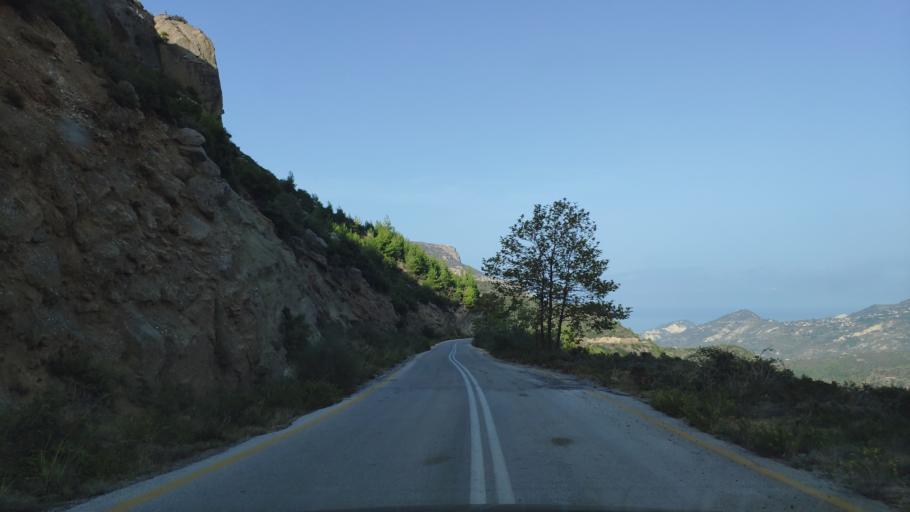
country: GR
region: West Greece
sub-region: Nomos Achaias
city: Aiyira
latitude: 38.0640
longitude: 22.3780
